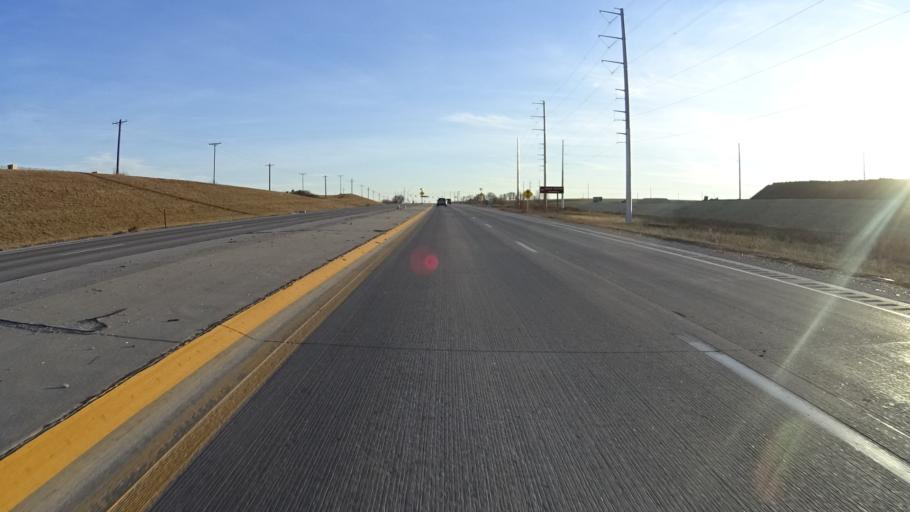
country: US
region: Nebraska
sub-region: Sarpy County
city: Chalco
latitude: 41.1366
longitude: -96.1392
